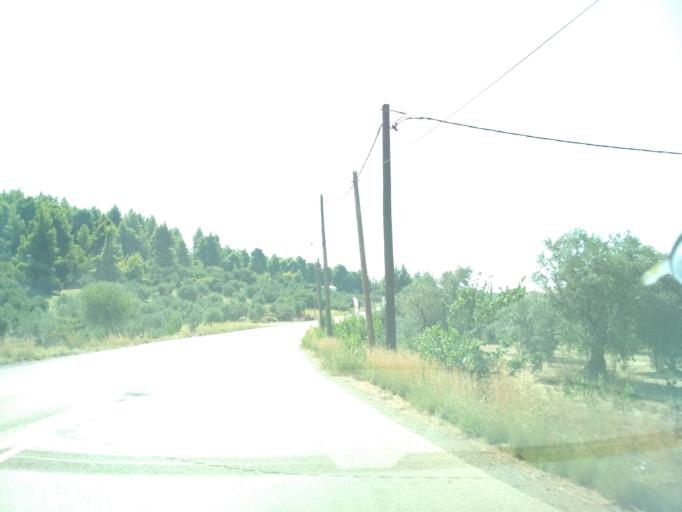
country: GR
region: Central Greece
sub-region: Nomos Evvoias
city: Roviai
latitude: 38.8287
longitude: 23.2241
